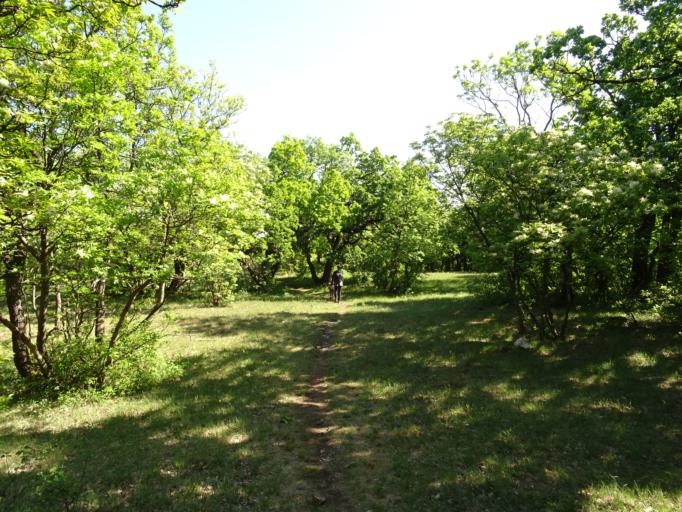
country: HU
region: Fejer
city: Csakvar
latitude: 47.3972
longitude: 18.4384
